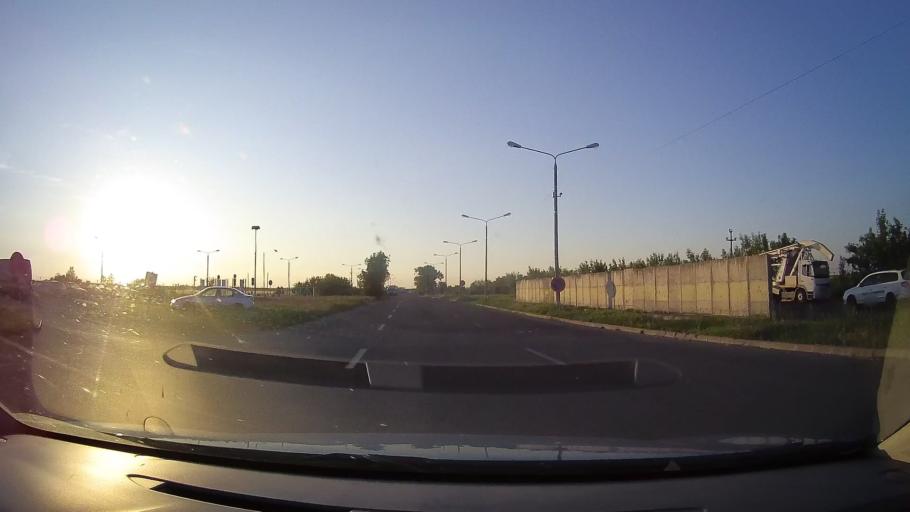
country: RO
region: Timis
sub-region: Comuna Moravita
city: Moravita
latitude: 45.2333
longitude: 21.2716
